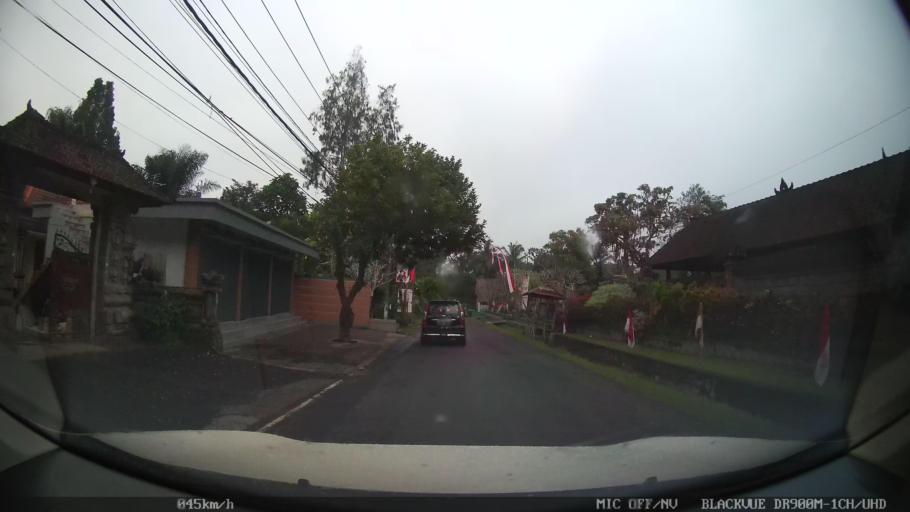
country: ID
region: Bali
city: Banjar Ponggang
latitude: -8.3807
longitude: 115.2656
